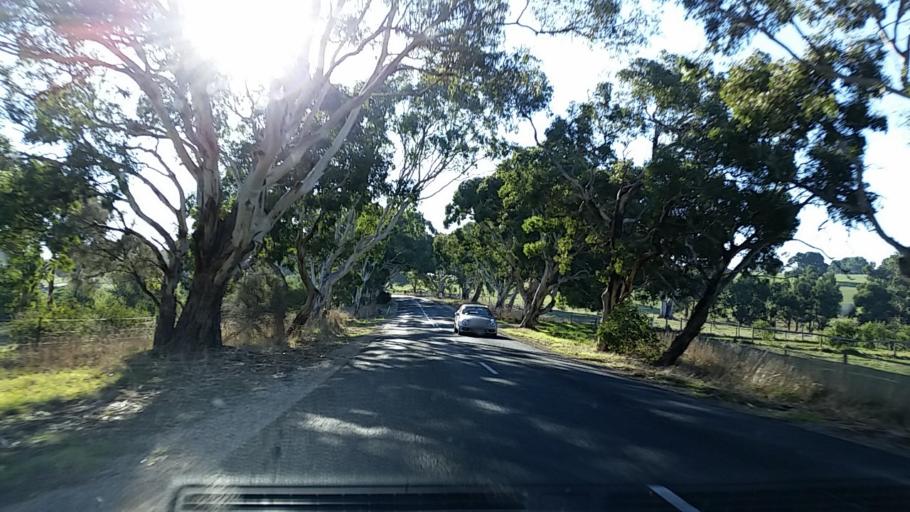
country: AU
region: South Australia
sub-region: Mount Barker
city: Mount Barker
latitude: -35.1308
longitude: 138.9120
